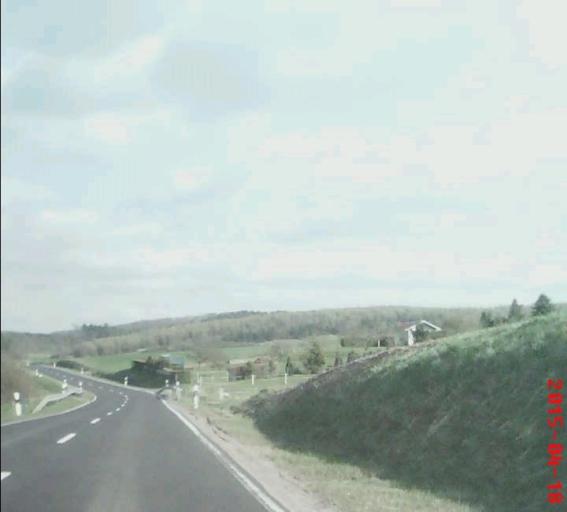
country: DE
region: Thuringia
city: Kallmerode
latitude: 51.3745
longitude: 10.2854
